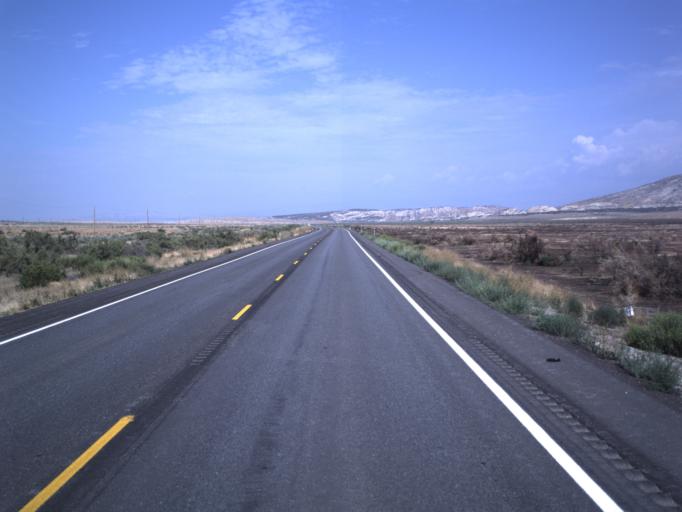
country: US
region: Utah
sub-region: Uintah County
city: Naples
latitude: 40.2961
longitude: -109.1825
